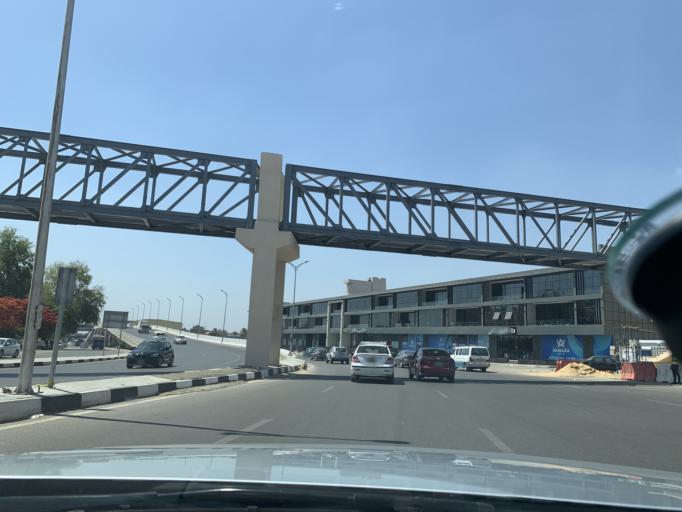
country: EG
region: Muhafazat al Qahirah
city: Cairo
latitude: 30.0915
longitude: 31.3484
